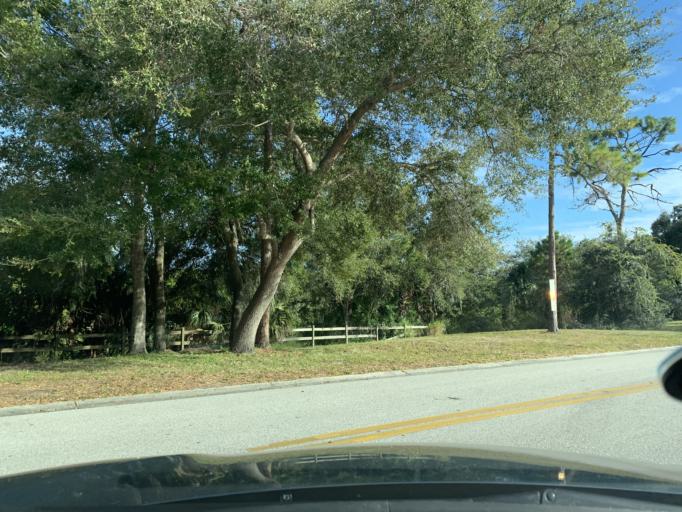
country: US
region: Florida
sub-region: Pinellas County
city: Kenneth City
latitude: 27.8251
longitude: -82.7443
